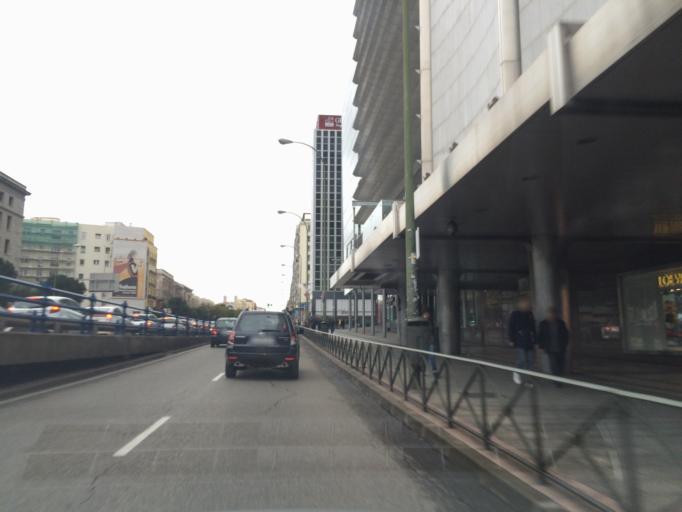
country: ES
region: Madrid
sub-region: Provincia de Madrid
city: Chamberi
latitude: 40.4465
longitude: -3.6935
